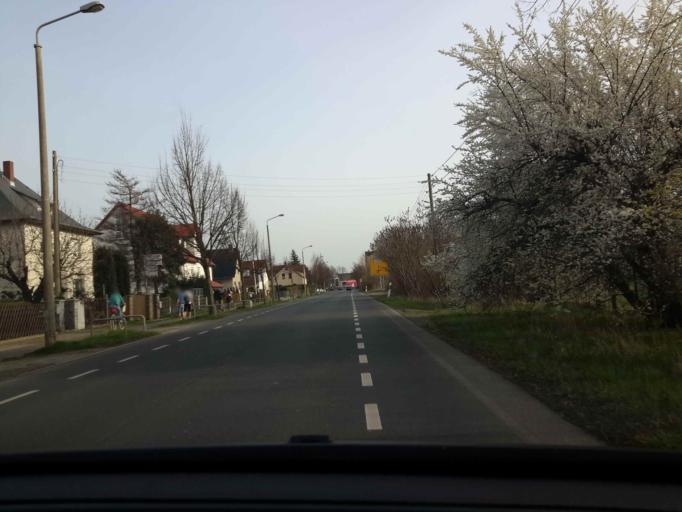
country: DE
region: Saxony
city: Rackwitz
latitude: 51.3992
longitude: 12.3693
